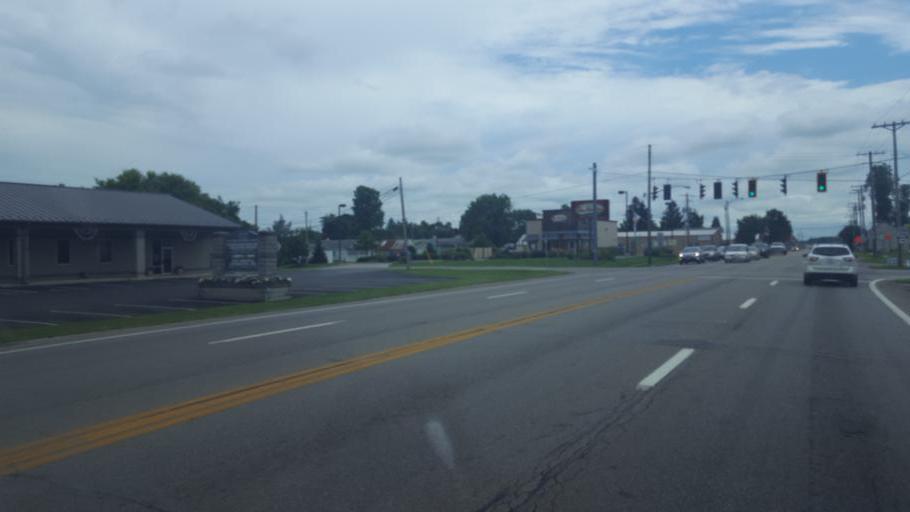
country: US
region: Ohio
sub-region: Pickaway County
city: South Bloomfield
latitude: 39.7191
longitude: -82.9868
